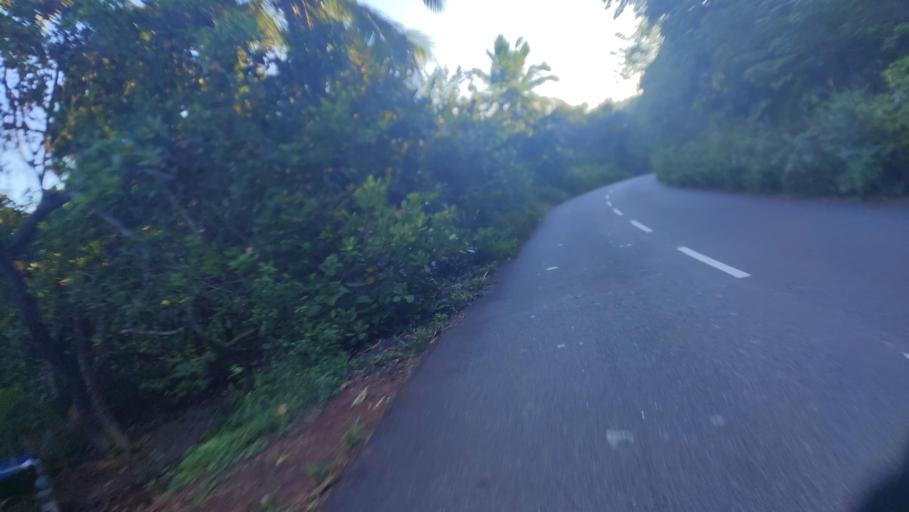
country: IN
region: Kerala
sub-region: Kasaragod District
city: Kasaragod
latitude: 12.4425
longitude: 75.0979
